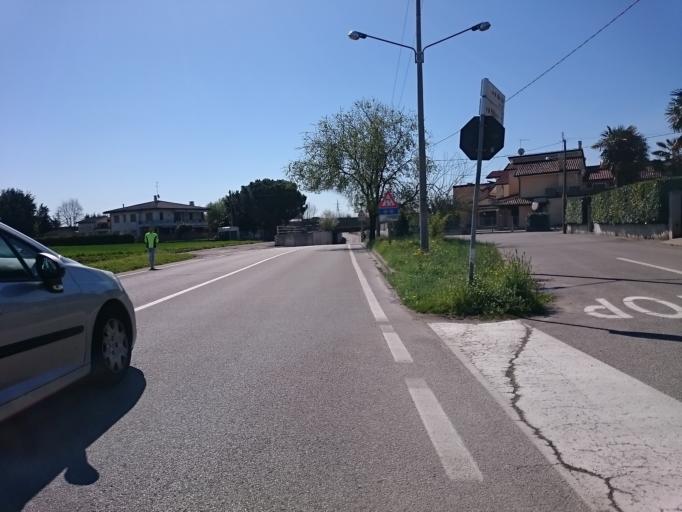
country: IT
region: Veneto
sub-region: Provincia di Padova
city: Ponte San Nicolo
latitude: 45.3737
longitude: 11.9047
